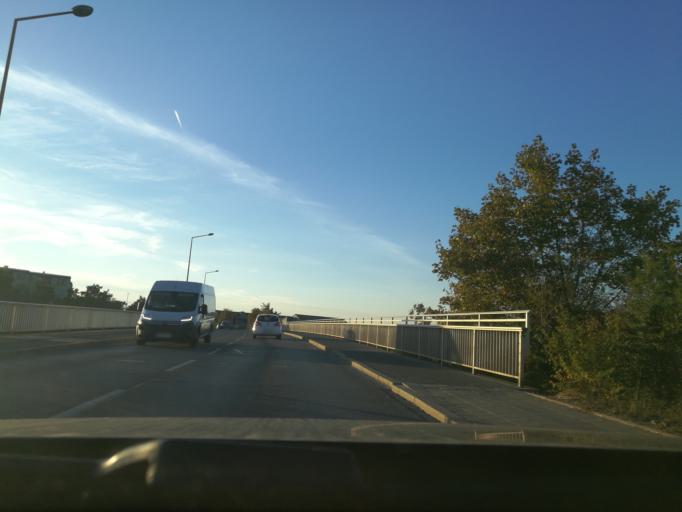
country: DE
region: Bavaria
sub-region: Regierungsbezirk Mittelfranken
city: Furth
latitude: 49.4915
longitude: 10.9443
